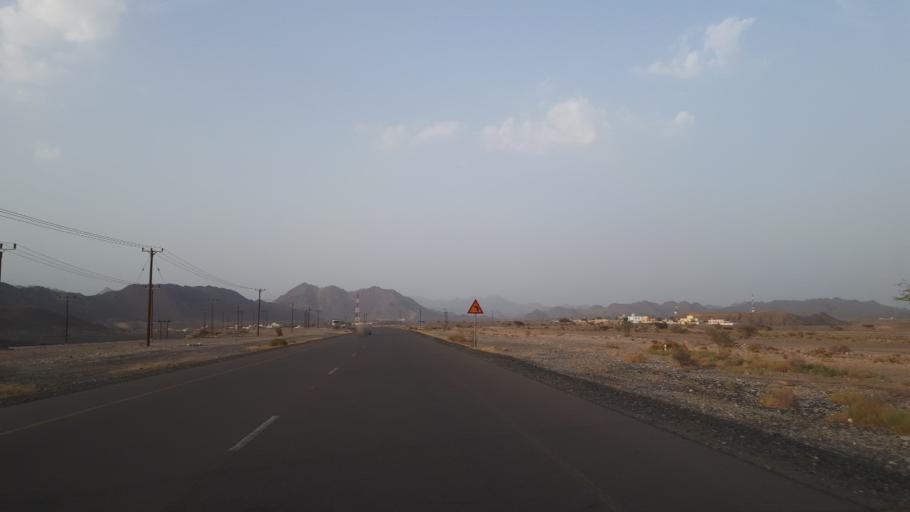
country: OM
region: Al Batinah
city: Rustaq
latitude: 23.3905
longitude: 57.2314
